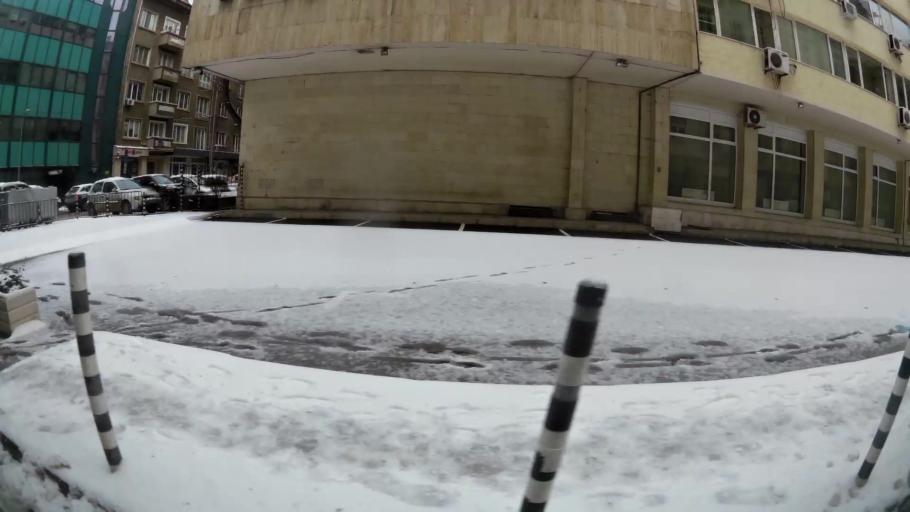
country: BG
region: Sofia-Capital
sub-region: Stolichna Obshtina
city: Sofia
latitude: 42.6986
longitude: 23.3255
